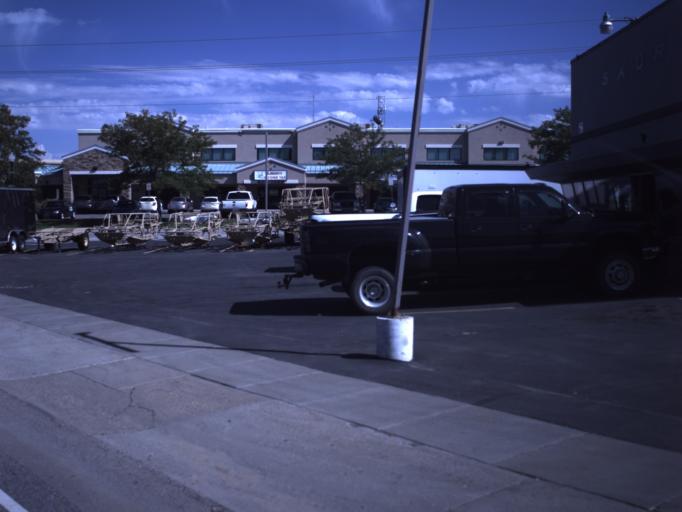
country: US
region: Utah
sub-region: Davis County
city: Clearfield
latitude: 41.1105
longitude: -112.0228
